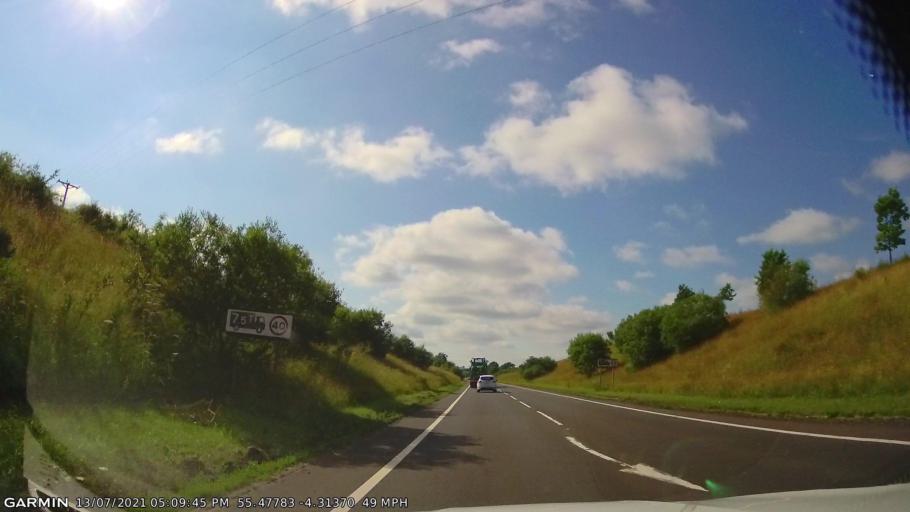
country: GB
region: Scotland
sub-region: East Ayrshire
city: Auchinleck
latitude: 55.4777
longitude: -4.3134
